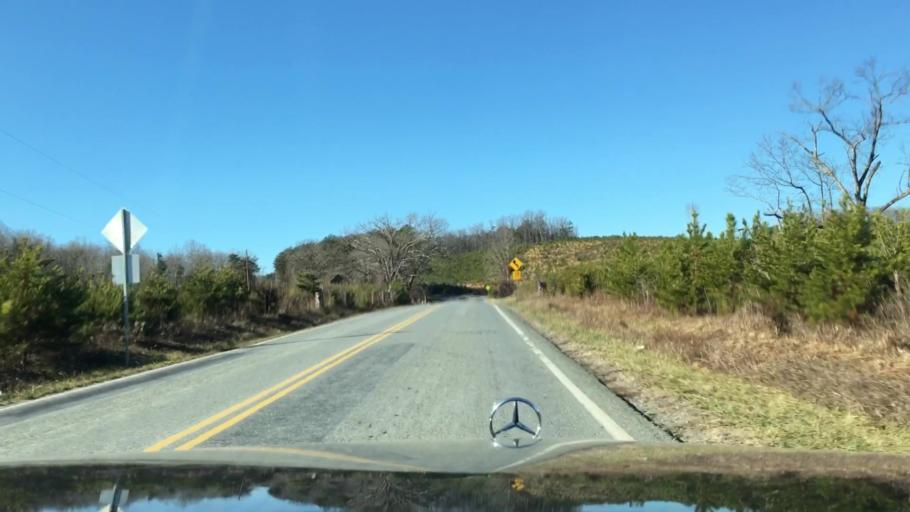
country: US
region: Virginia
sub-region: Pittsylvania County
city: Motley
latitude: 37.1537
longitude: -79.3880
